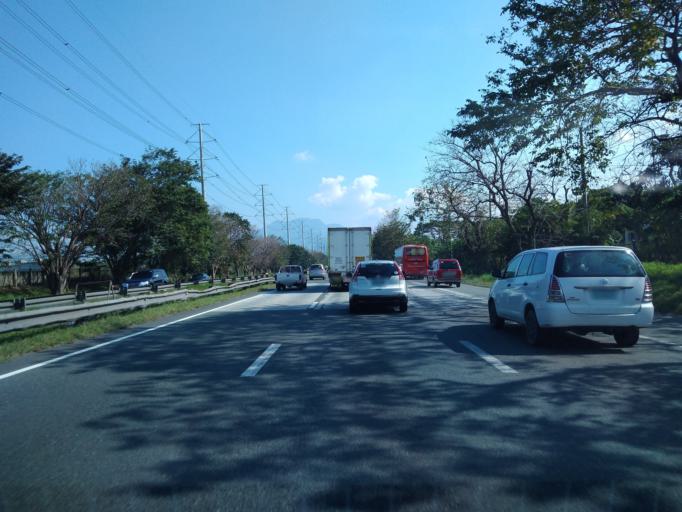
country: PH
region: Calabarzon
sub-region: Province of Laguna
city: Prinza
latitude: 14.2260
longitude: 121.1209
